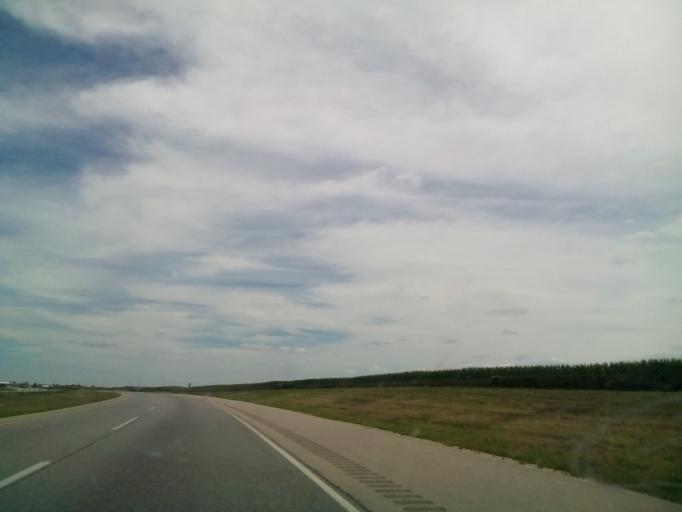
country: US
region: Illinois
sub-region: DeKalb County
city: Malta
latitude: 41.8996
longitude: -88.9535
